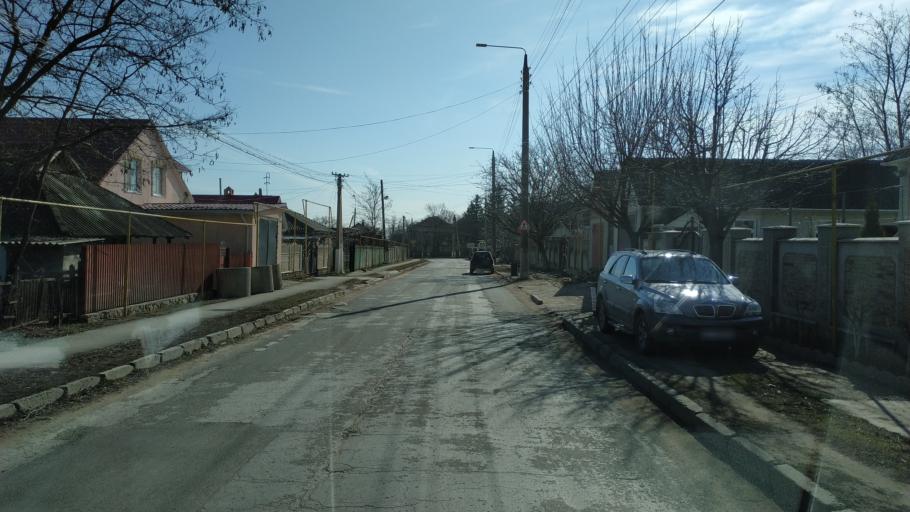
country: MD
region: Nisporeni
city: Nisporeni
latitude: 47.0804
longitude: 28.1674
